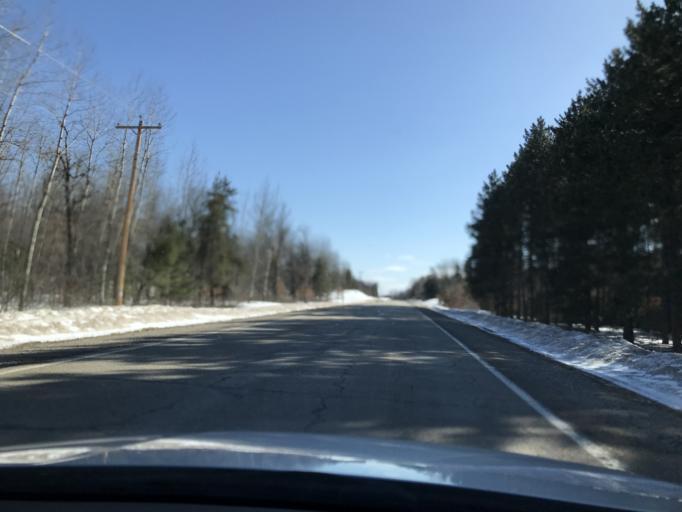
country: US
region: Wisconsin
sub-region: Marinette County
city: Niagara
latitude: 45.3465
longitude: -88.1014
